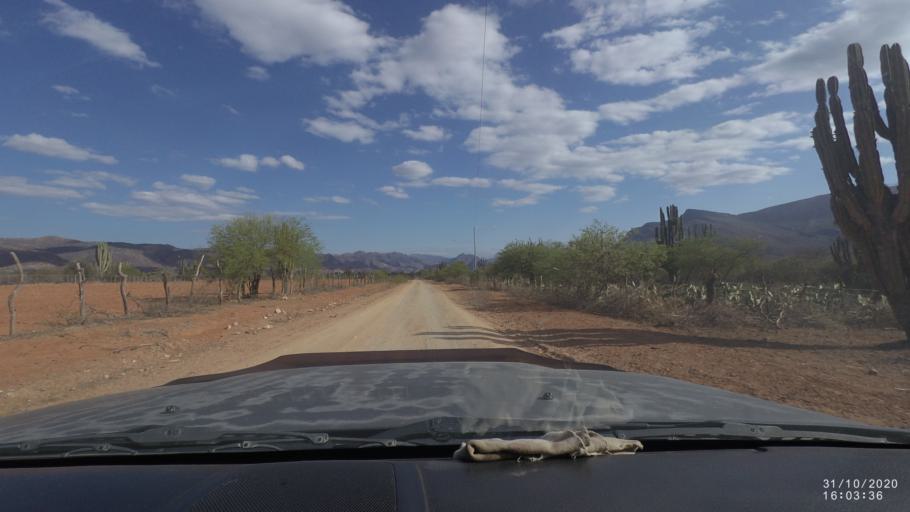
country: BO
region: Chuquisaca
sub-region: Provincia Zudanez
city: Mojocoya
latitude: -18.3533
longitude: -64.6524
